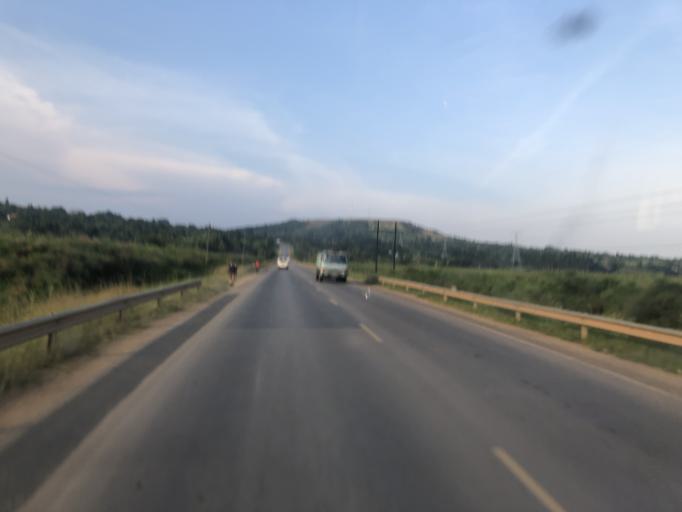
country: UG
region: Central Region
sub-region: Mpigi District
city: Mpigi
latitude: 0.1848
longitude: 32.2867
